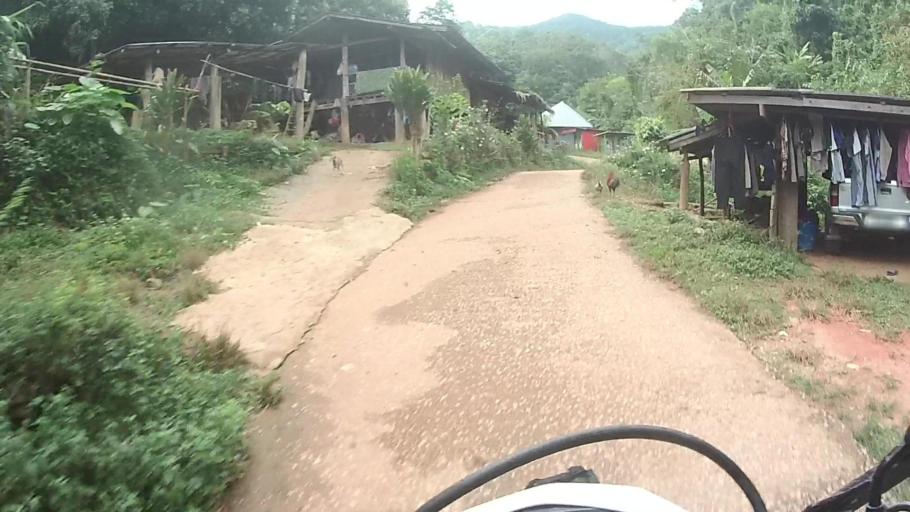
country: TH
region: Lampang
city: Wang Nuea
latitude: 19.0243
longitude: 99.4799
